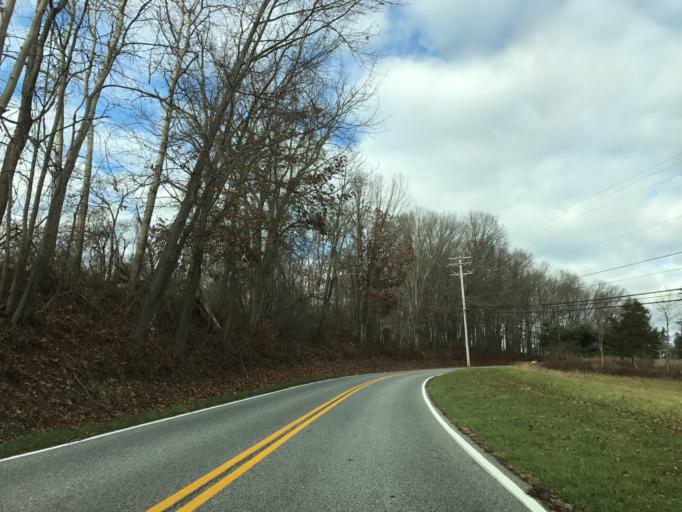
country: US
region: Pennsylvania
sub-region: York County
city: New Freedom
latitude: 39.6348
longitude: -76.6326
